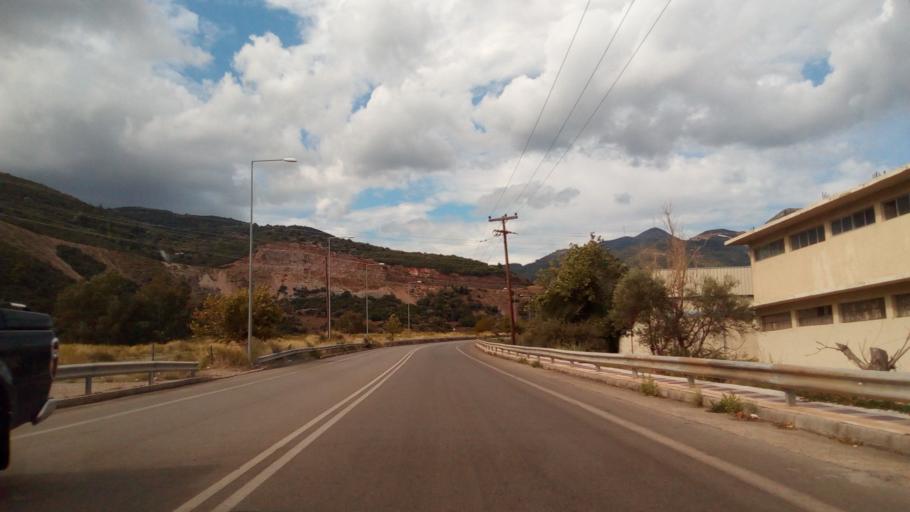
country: GR
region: West Greece
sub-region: Nomos Aitolias kai Akarnanias
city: Nafpaktos
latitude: 38.4006
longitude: 21.8430
